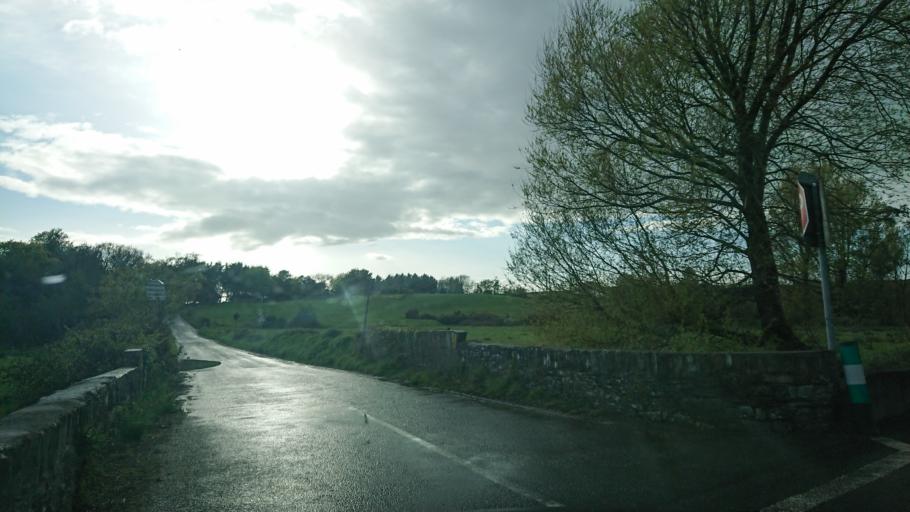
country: IE
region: Munster
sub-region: Waterford
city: Waterford
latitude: 52.2209
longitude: -7.1276
